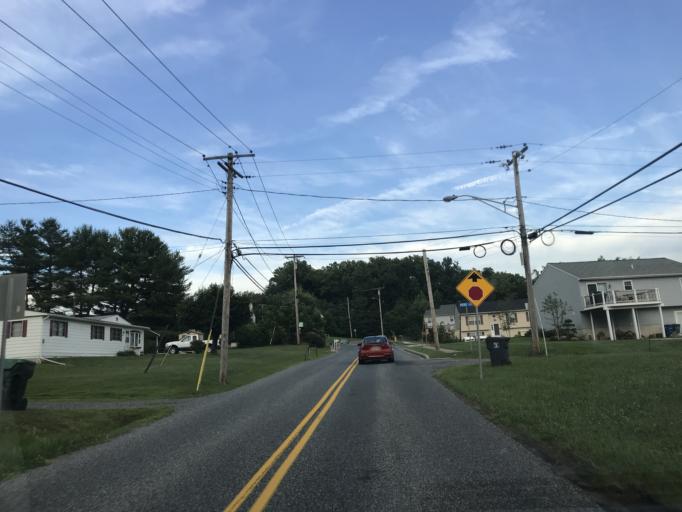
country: US
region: Maryland
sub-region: Harford County
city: Aberdeen
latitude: 39.5154
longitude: -76.1900
